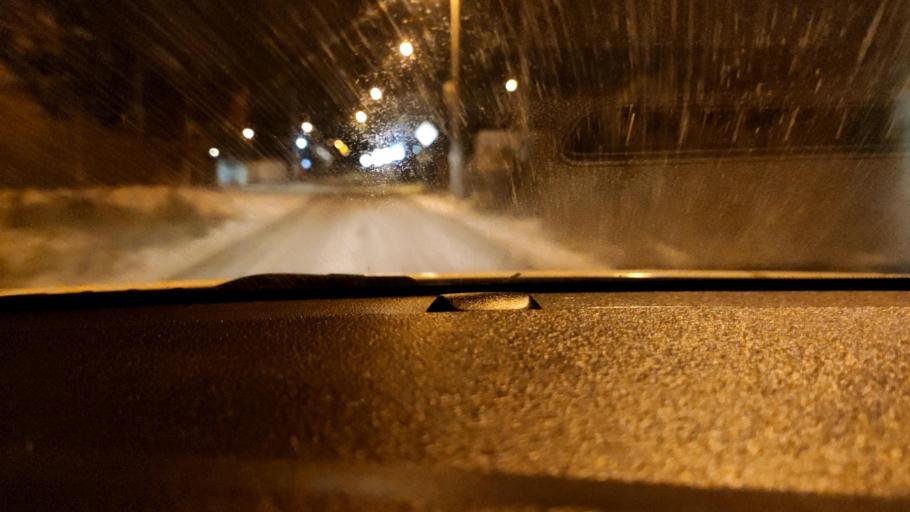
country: RU
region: Tatarstan
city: Osinovo
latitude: 55.8283
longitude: 48.8586
